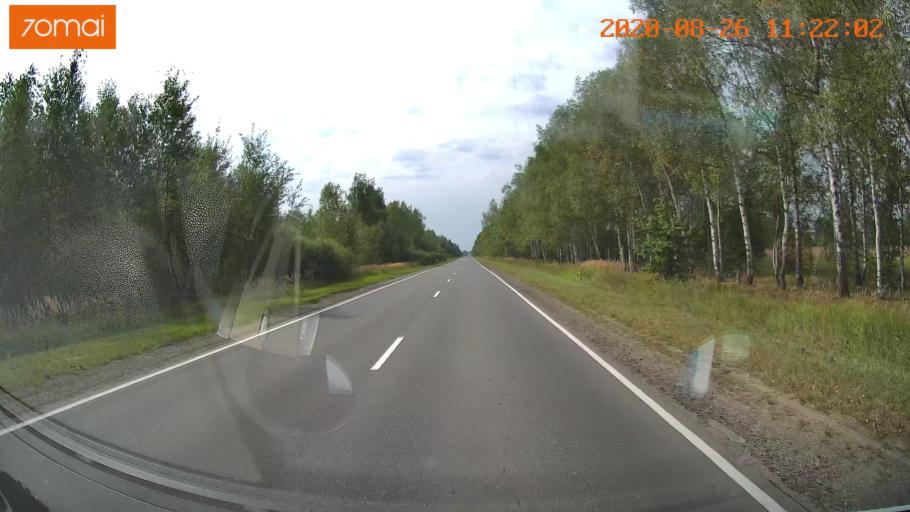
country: RU
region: Rjazan
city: Shilovo
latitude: 54.3689
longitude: 41.0343
